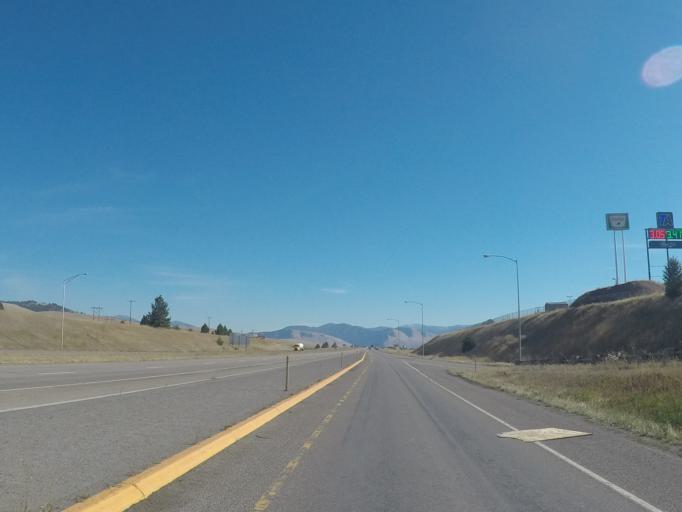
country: US
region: Montana
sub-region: Missoula County
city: Orchard Homes
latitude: 46.9500
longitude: -114.1294
